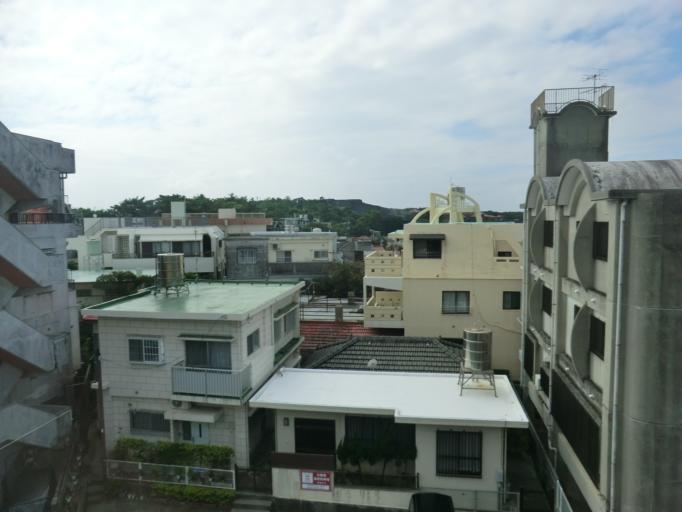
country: JP
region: Okinawa
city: Naha-shi
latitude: 26.2194
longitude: 127.7234
